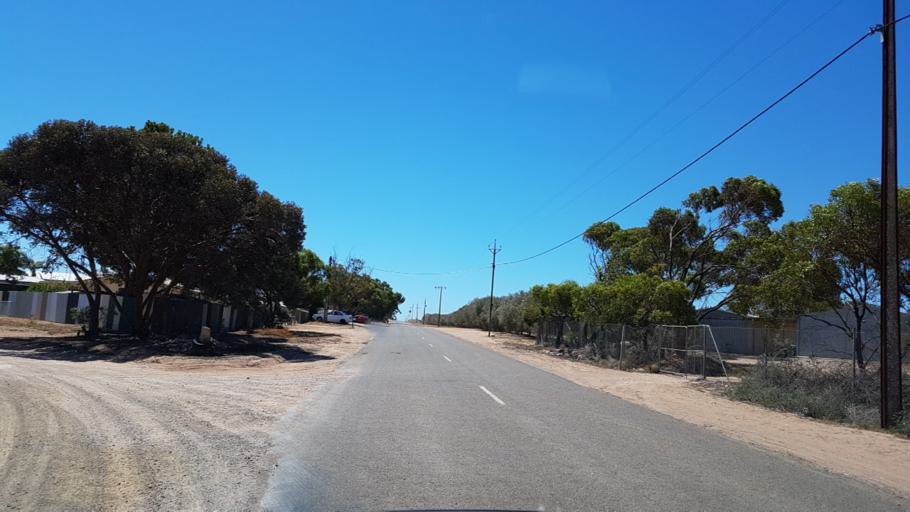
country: AU
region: South Australia
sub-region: Copper Coast
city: Wallaroo
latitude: -34.0519
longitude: 137.5930
